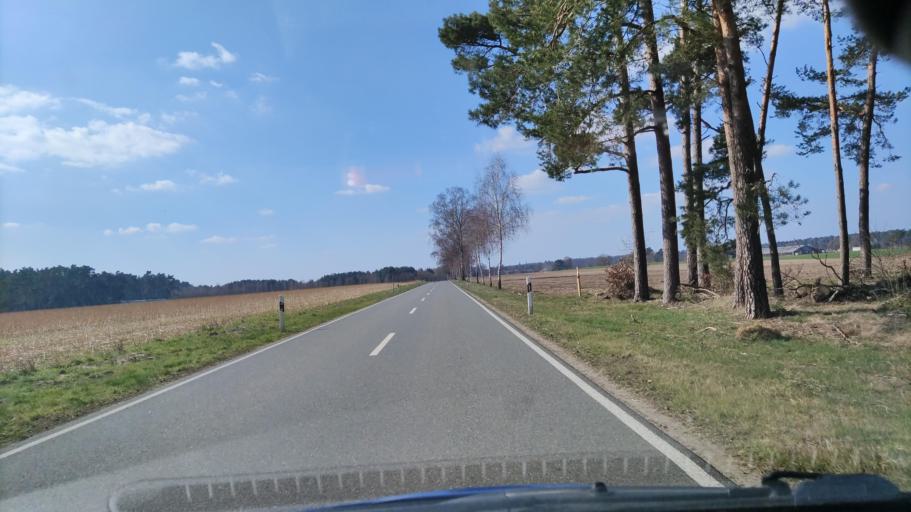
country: DE
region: Lower Saxony
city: Trebel
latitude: 53.0288
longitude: 11.3203
